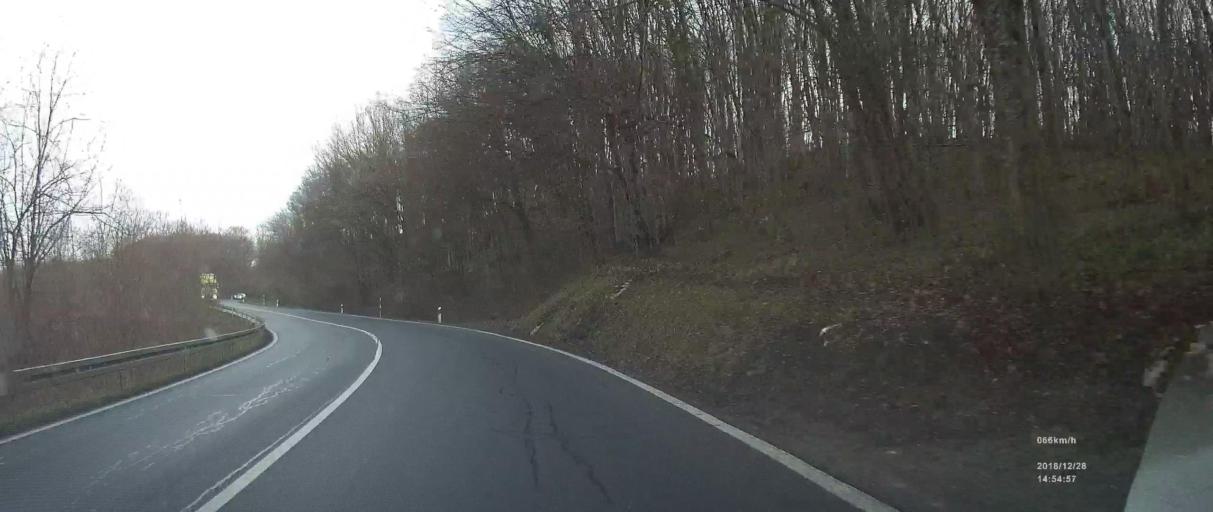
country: HR
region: Karlovacka
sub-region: Grad Karlovac
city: Karlovac
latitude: 45.4540
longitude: 15.4239
